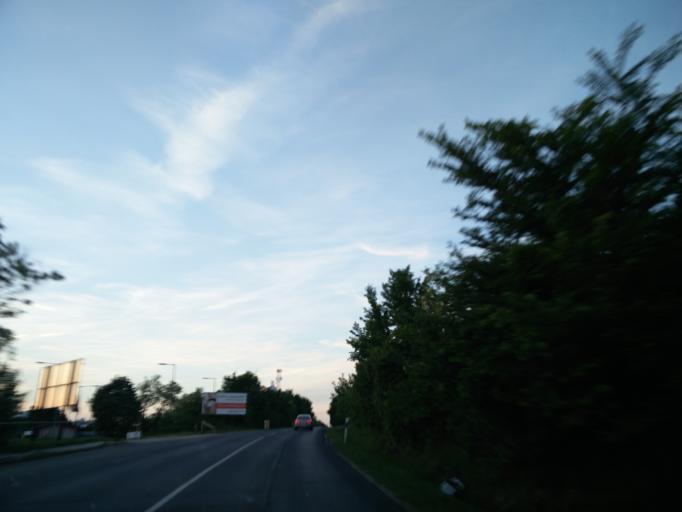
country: HU
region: Pest
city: Toeroekbalint
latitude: 47.4639
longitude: 18.9006
